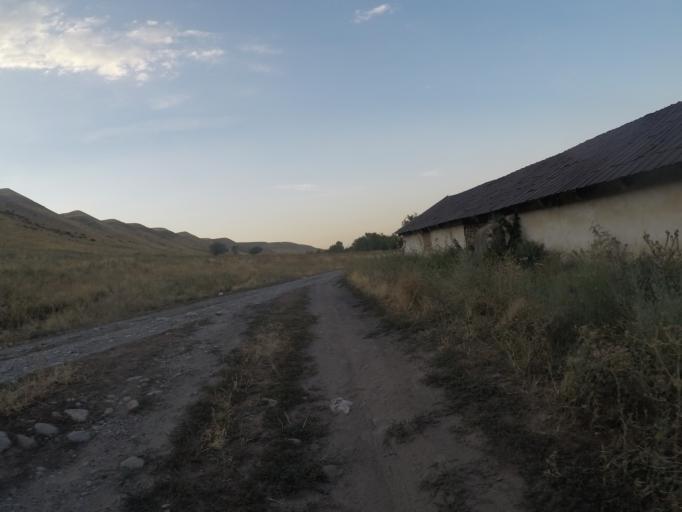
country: KG
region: Chuy
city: Bishkek
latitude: 42.7659
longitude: 74.6380
